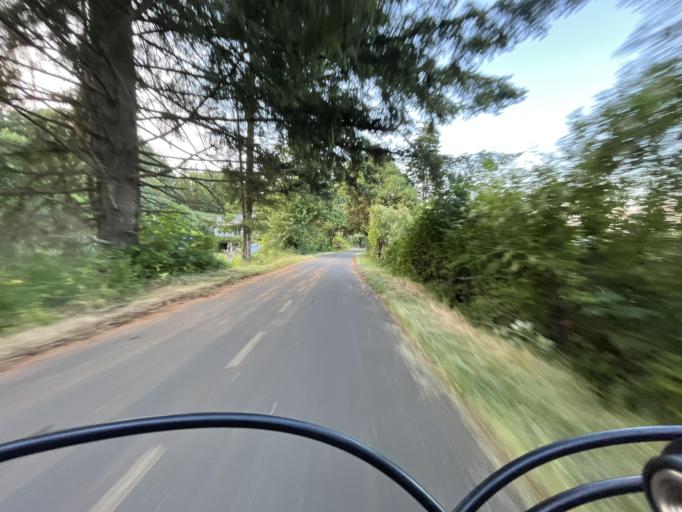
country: CA
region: British Columbia
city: Colwood
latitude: 48.4523
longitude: -123.4705
